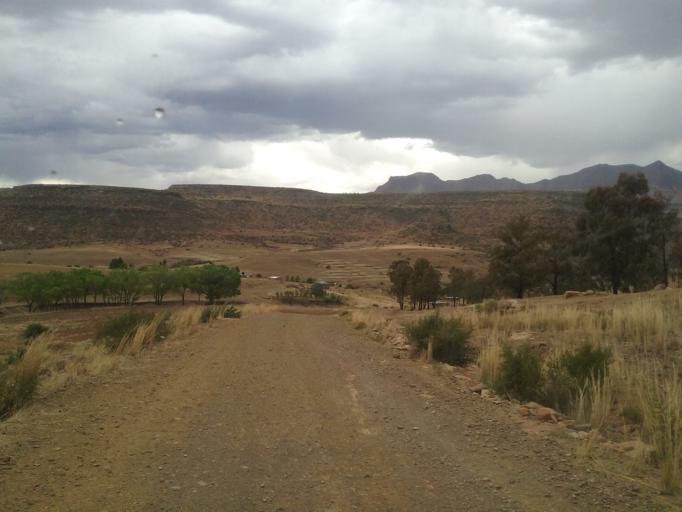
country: LS
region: Quthing
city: Quthing
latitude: -30.3006
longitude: 27.8130
